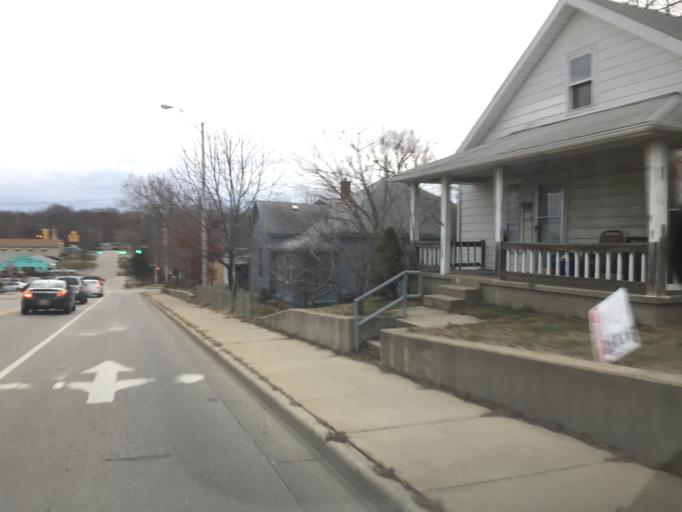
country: US
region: Indiana
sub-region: Monroe County
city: Bloomington
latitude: 39.1667
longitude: -86.5486
